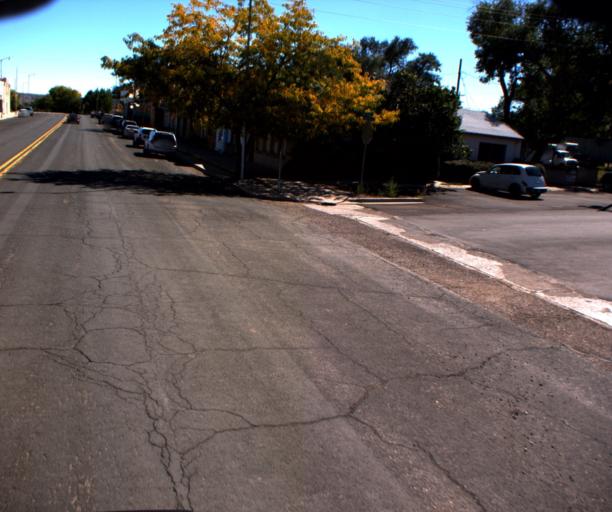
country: US
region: Arizona
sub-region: Apache County
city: Saint Johns
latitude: 34.5062
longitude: -109.3630
